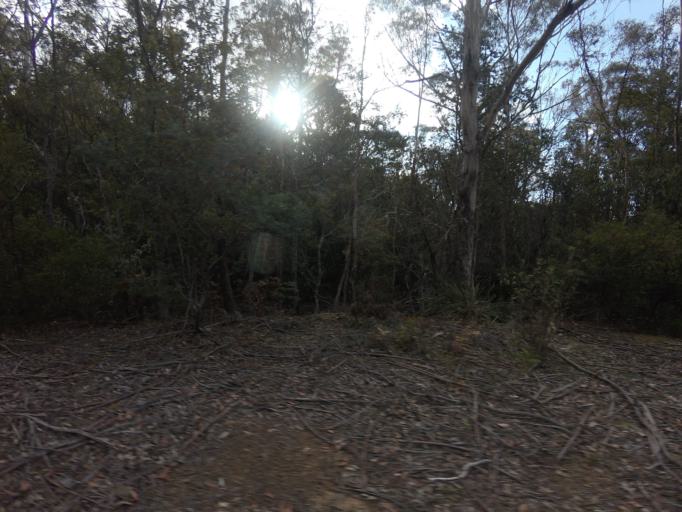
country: AU
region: Tasmania
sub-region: Break O'Day
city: St Helens
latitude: -41.8621
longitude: 148.0234
